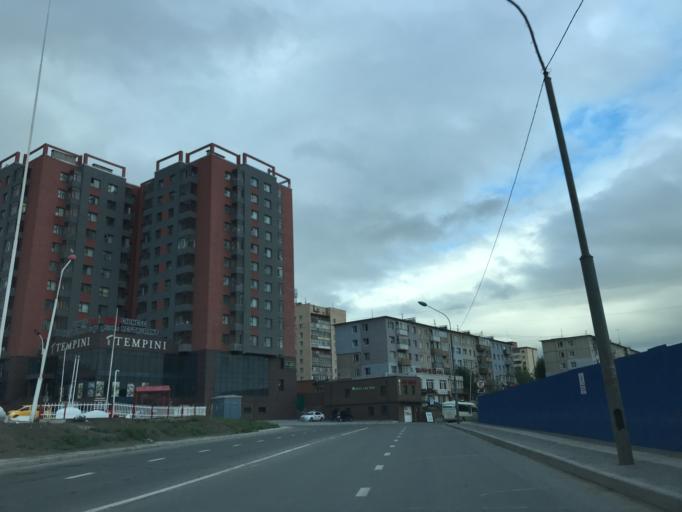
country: MN
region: Ulaanbaatar
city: Ulaanbaatar
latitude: 47.9282
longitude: 106.9360
